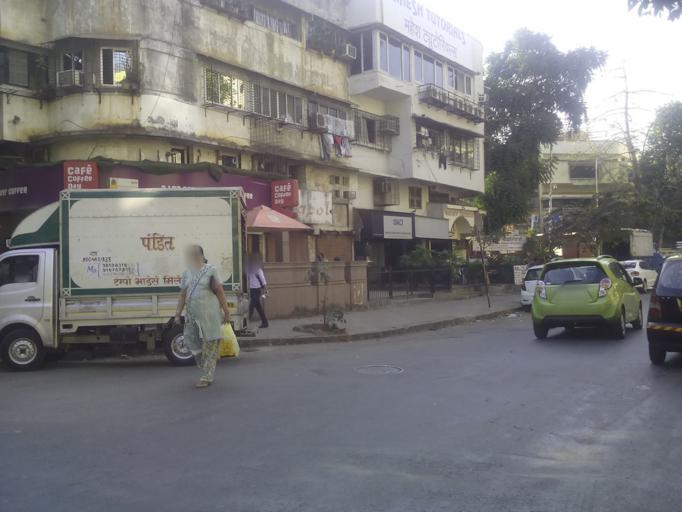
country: IN
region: Maharashtra
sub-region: Mumbai Suburban
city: Mumbai
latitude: 19.0435
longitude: 72.8624
